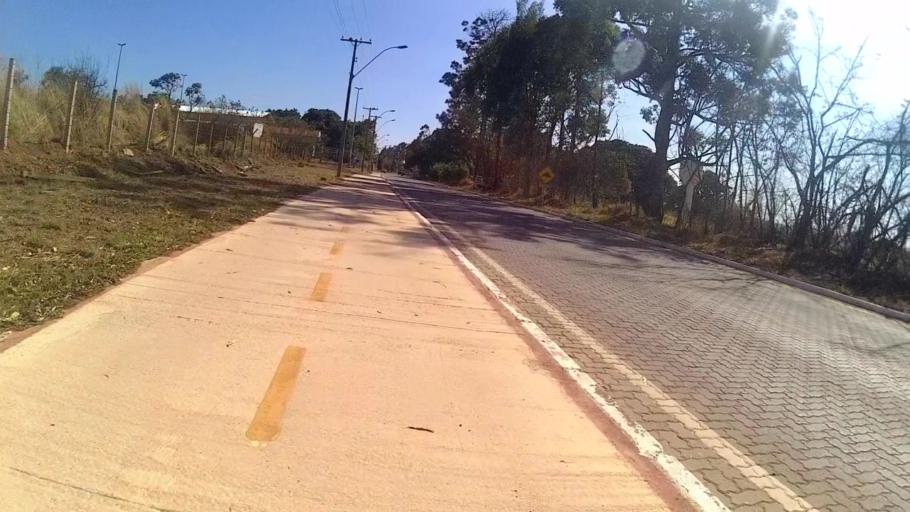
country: BR
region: Federal District
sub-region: Brasilia
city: Brasilia
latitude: -15.6472
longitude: -47.8898
